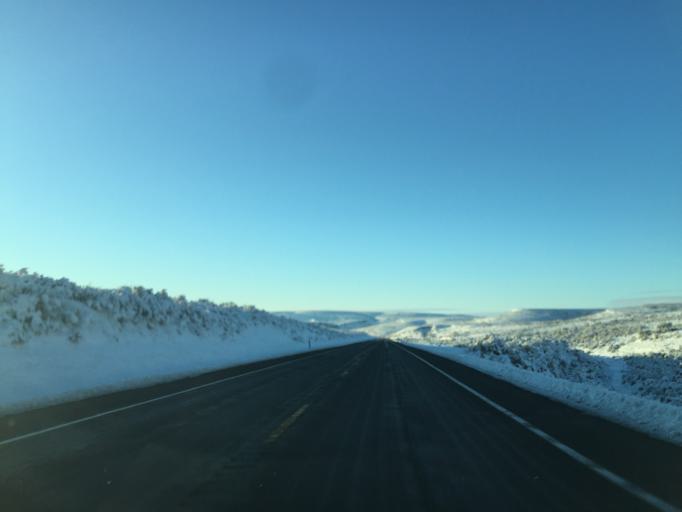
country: US
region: Washington
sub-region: Grant County
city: Soap Lake
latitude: 47.6031
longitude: -119.6263
